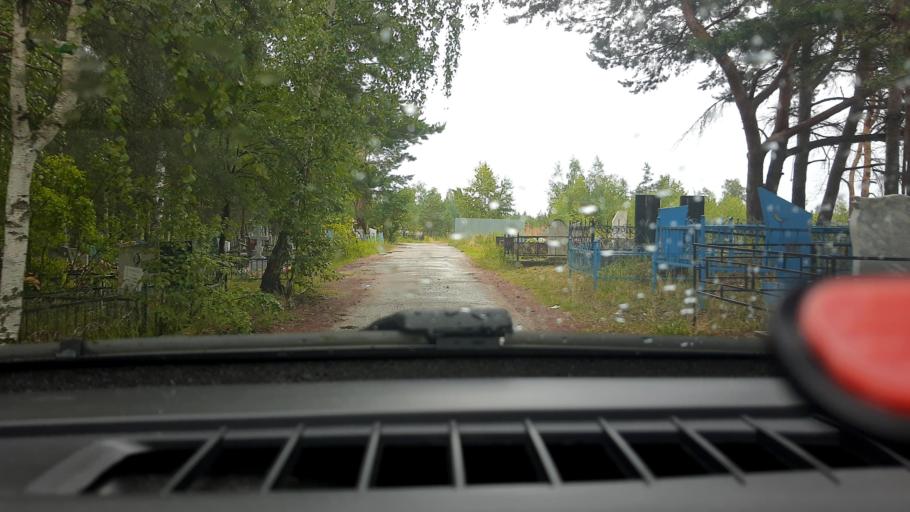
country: RU
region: Nizjnij Novgorod
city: Gorbatovka
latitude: 56.3509
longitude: 43.7800
